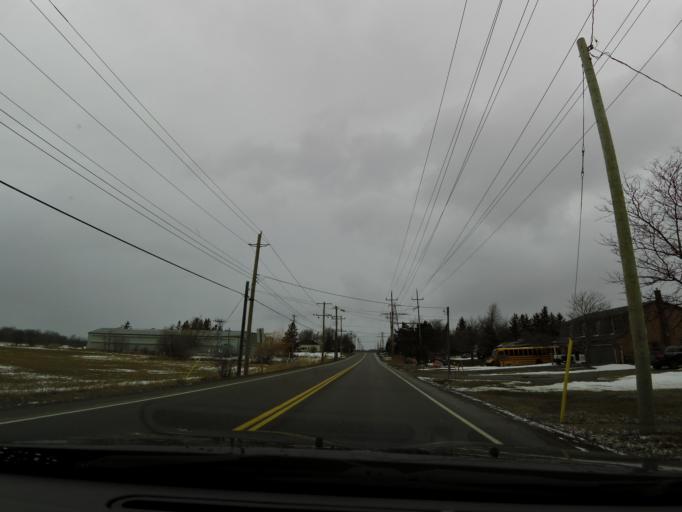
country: CA
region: Ontario
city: Ancaster
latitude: 43.2890
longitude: -79.9460
